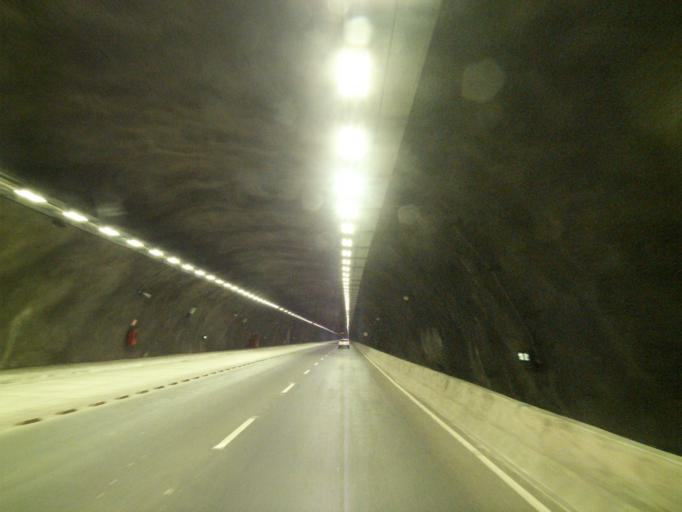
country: BR
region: Rio de Janeiro
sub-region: Niteroi
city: Niteroi
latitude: -22.9333
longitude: -43.0954
